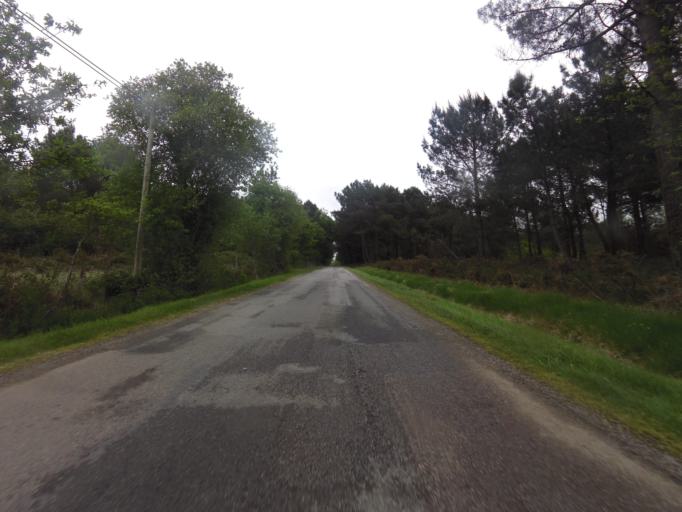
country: FR
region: Brittany
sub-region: Departement du Morbihan
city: Plougoumelen
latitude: 47.6361
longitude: -2.9055
